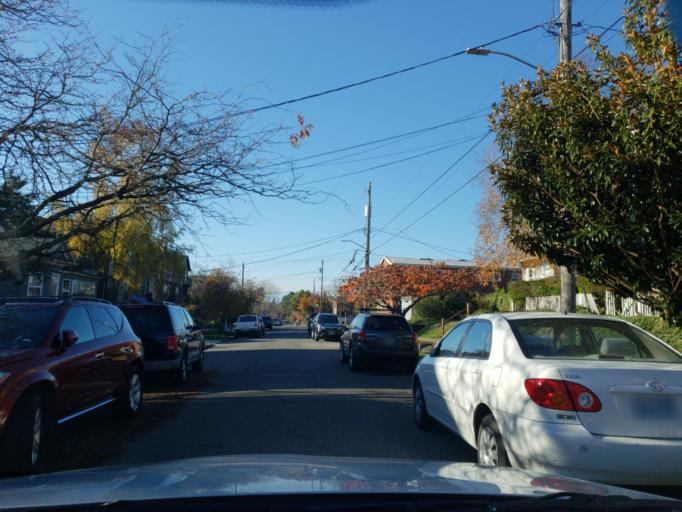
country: US
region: Washington
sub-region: King County
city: Seattle
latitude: 47.6746
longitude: -122.3863
